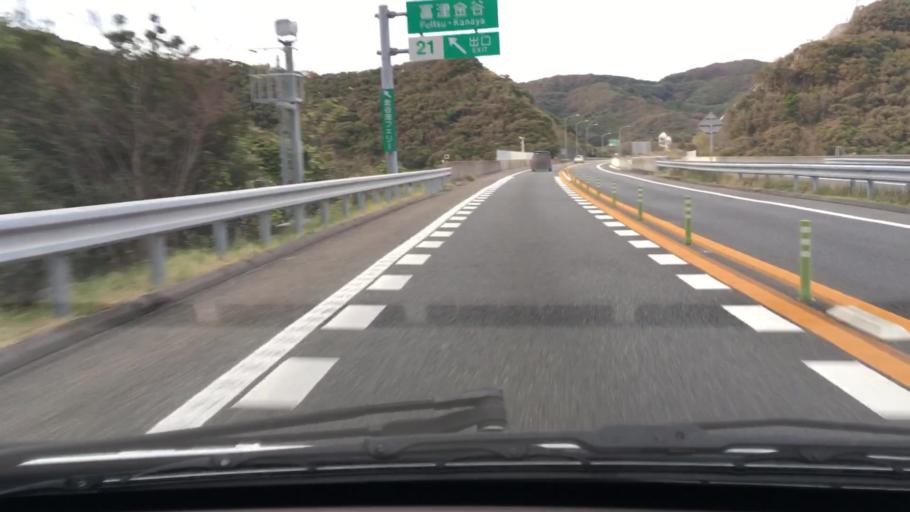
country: JP
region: Chiba
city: Futtsu
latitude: 35.1653
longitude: 139.8314
